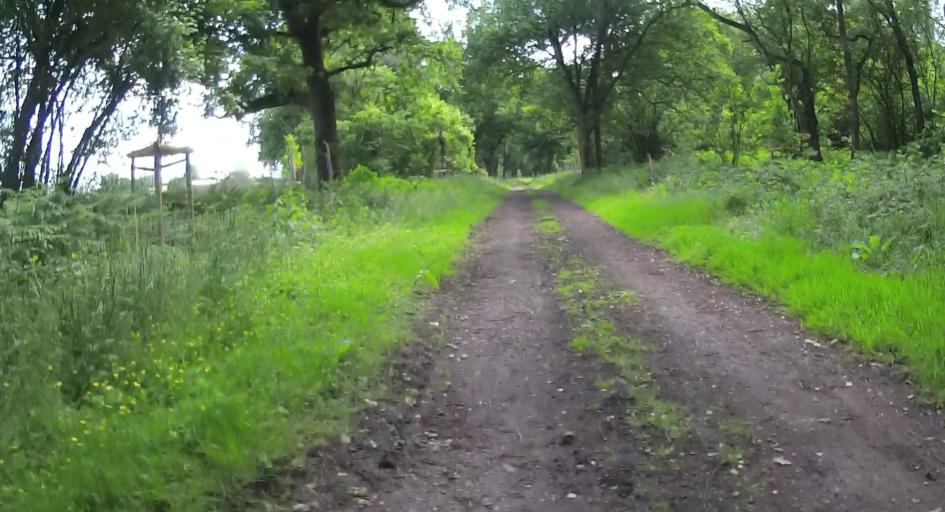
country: GB
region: England
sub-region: Hampshire
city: Basingstoke
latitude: 51.1916
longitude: -1.1660
